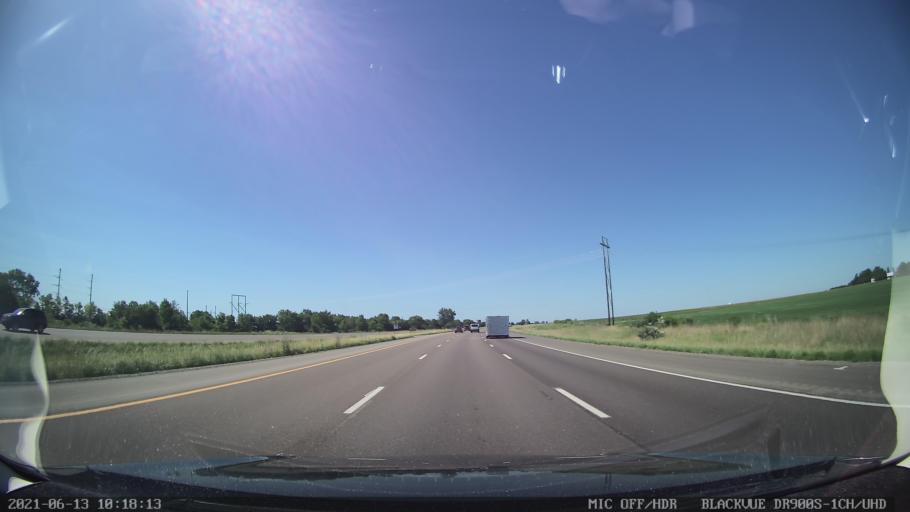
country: US
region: Illinois
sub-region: Logan County
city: Lincoln
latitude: 40.1010
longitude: -89.4176
